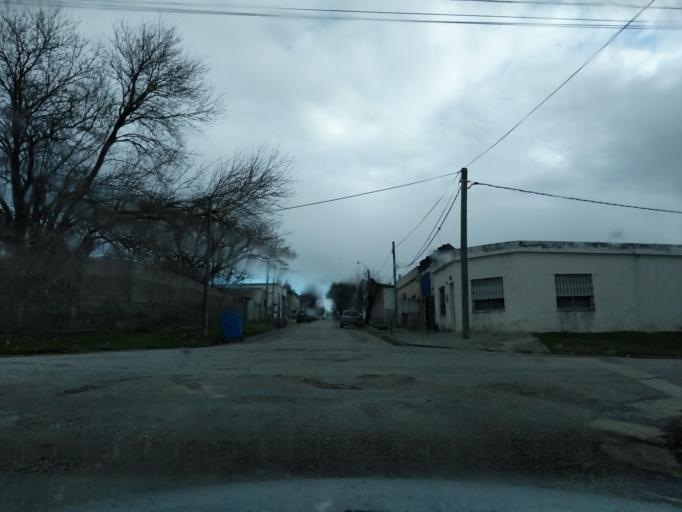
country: UY
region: Florida
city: Florida
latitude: -34.0932
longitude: -56.2109
